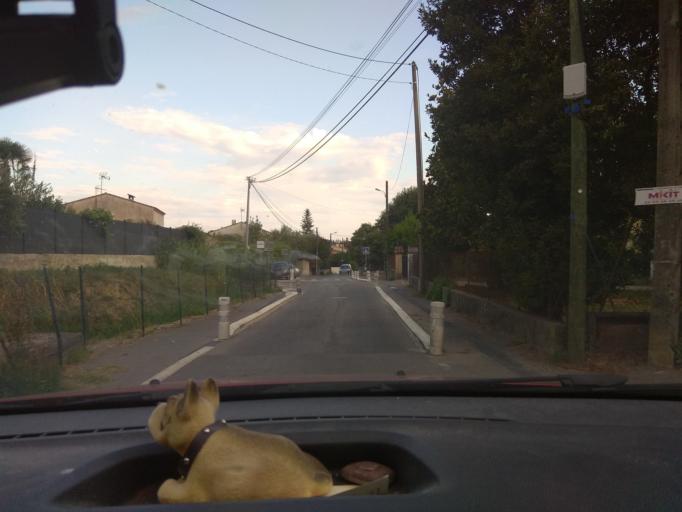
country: FR
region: Provence-Alpes-Cote d'Azur
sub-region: Departement des Alpes-Maritimes
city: La Colle-sur-Loup
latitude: 43.6774
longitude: 7.1083
